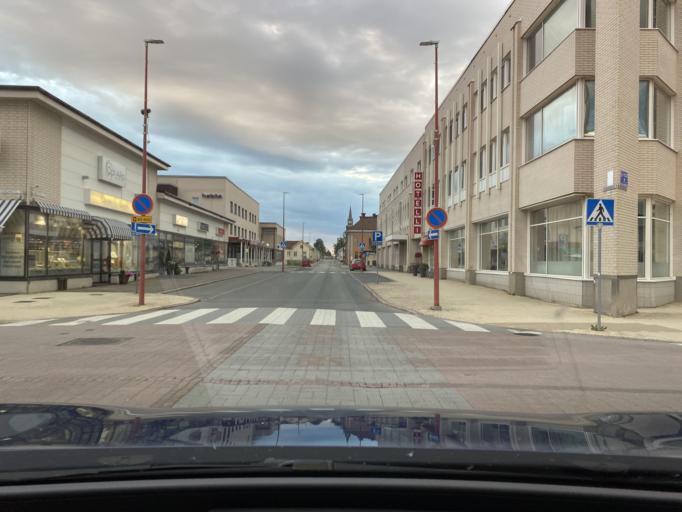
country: FI
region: Northern Ostrobothnia
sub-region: Raahe
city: Raahe
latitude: 64.6845
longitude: 24.4792
